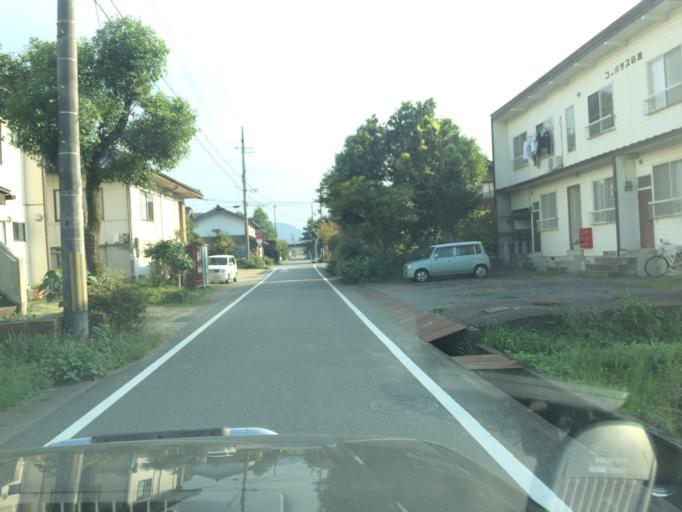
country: JP
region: Hyogo
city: Toyooka
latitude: 35.4779
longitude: 134.7774
